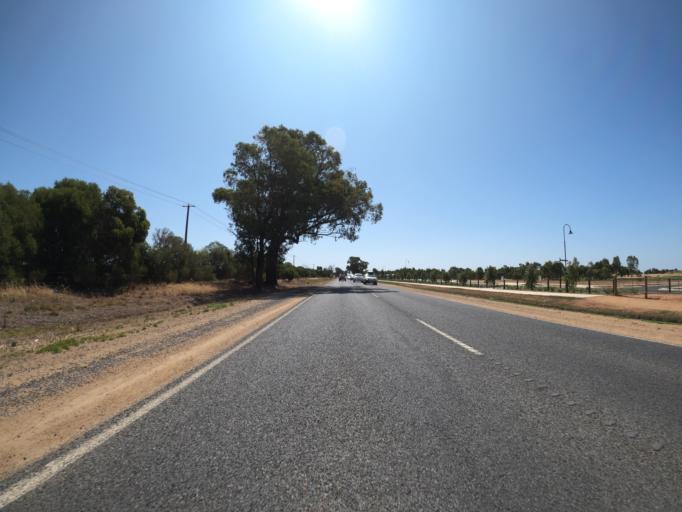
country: AU
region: Victoria
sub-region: Moira
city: Yarrawonga
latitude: -36.0140
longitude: 146.0410
